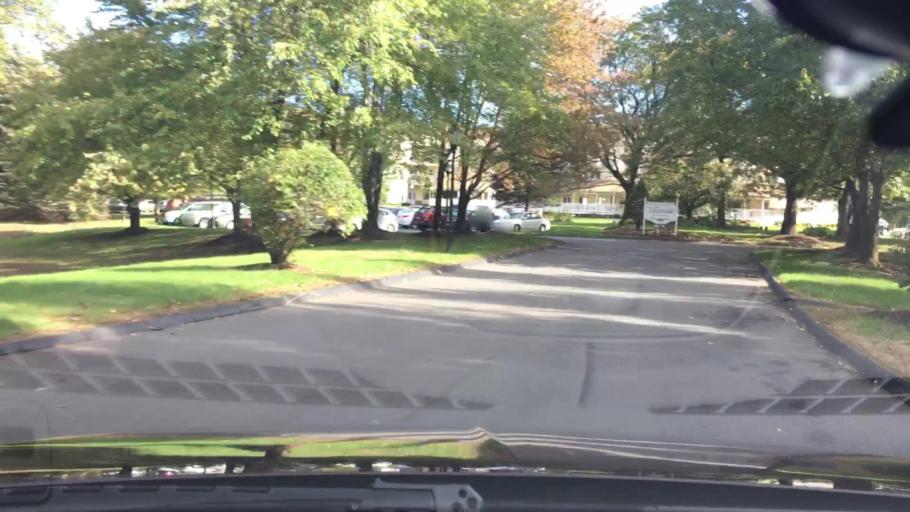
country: US
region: Connecticut
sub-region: Hartford County
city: Farmington
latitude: 41.7045
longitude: -72.8566
